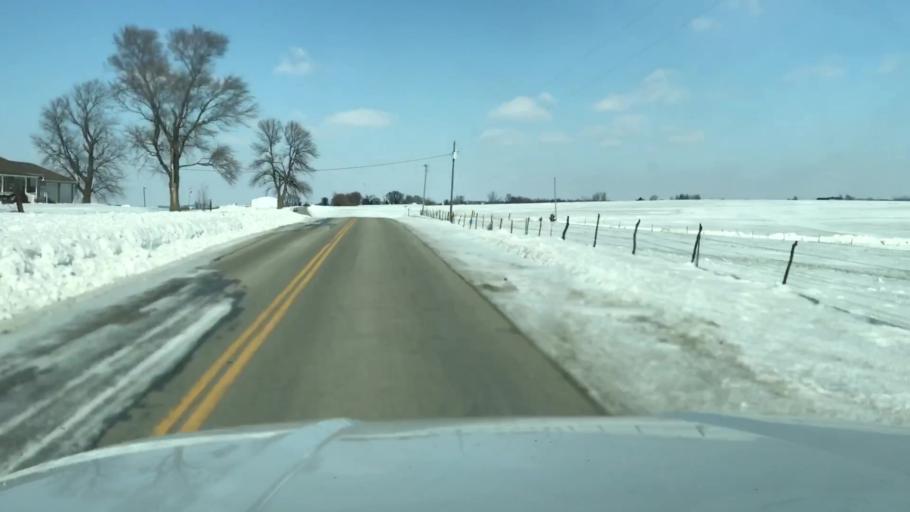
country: US
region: Missouri
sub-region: Nodaway County
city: Maryville
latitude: 40.3855
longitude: -94.7216
